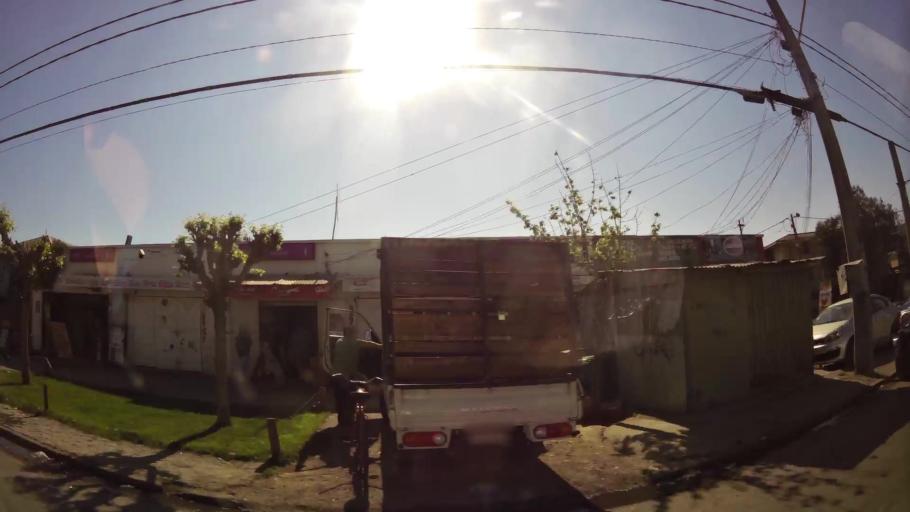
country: CL
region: Santiago Metropolitan
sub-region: Provincia de Maipo
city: San Bernardo
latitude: -33.5187
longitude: -70.7003
